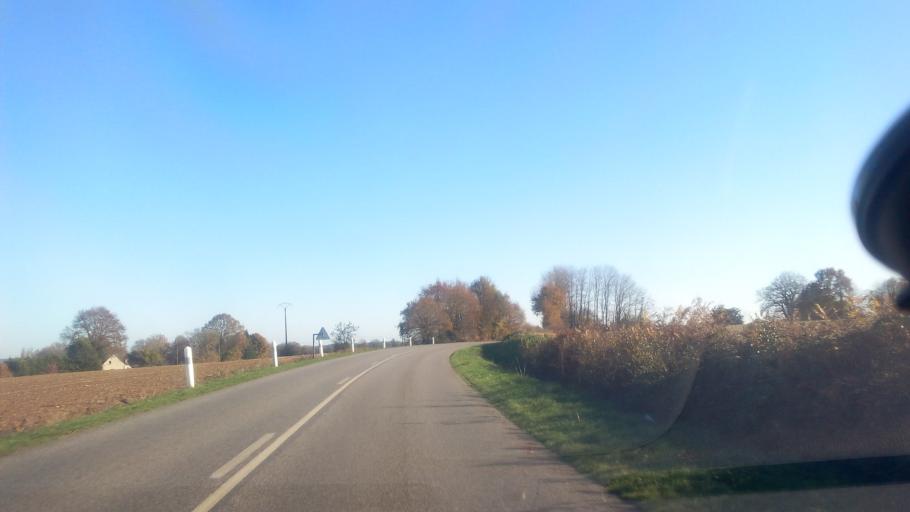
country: FR
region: Brittany
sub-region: Departement du Morbihan
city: Saint-Vincent-sur-Oust
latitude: 47.7133
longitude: -2.1802
